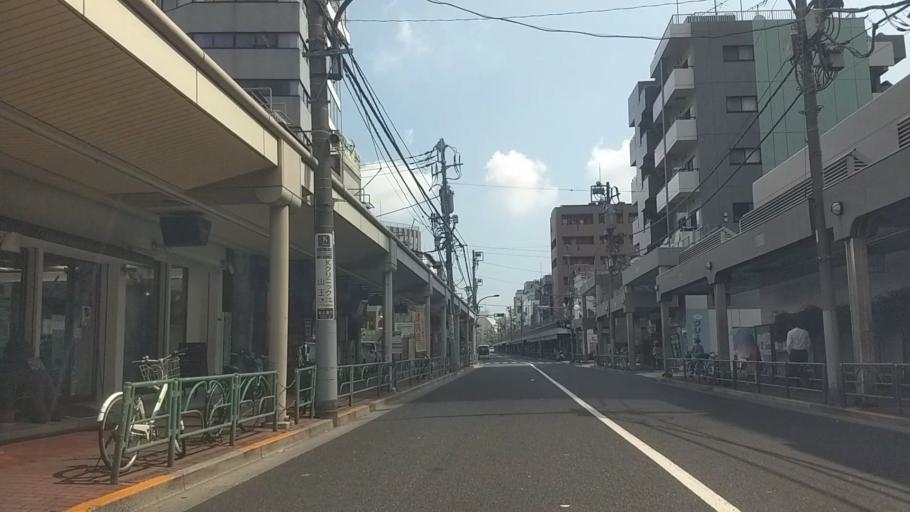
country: JP
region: Kanagawa
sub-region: Kawasaki-shi
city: Kawasaki
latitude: 35.5835
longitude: 139.7236
